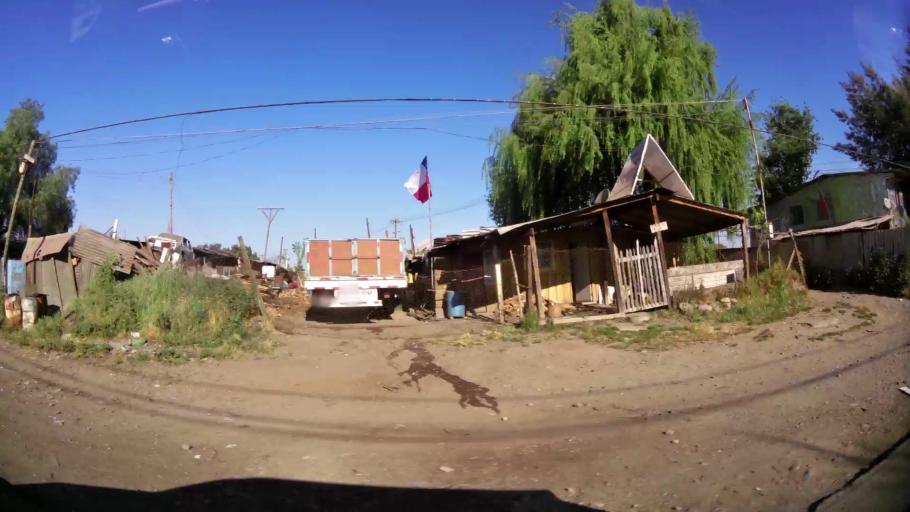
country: CL
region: Santiago Metropolitan
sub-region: Provincia de Talagante
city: Penaflor
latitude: -33.6095
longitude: -70.8605
